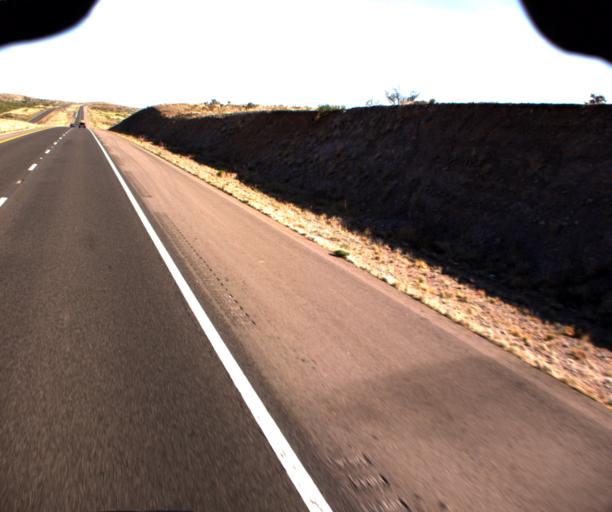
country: US
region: Arizona
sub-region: Cochise County
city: Willcox
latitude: 32.4274
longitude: -109.6629
